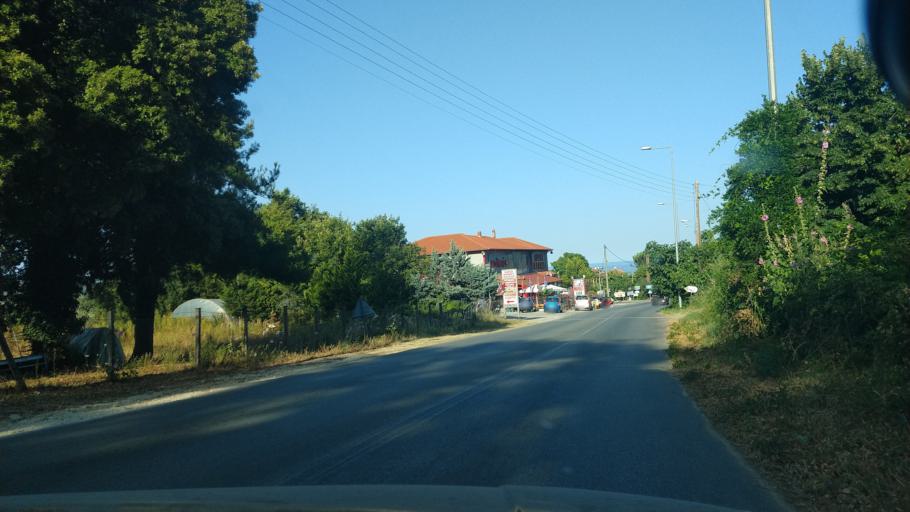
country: GR
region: East Macedonia and Thrace
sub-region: Nomos Kavalas
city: Potamia
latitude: 40.7157
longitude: 24.7386
